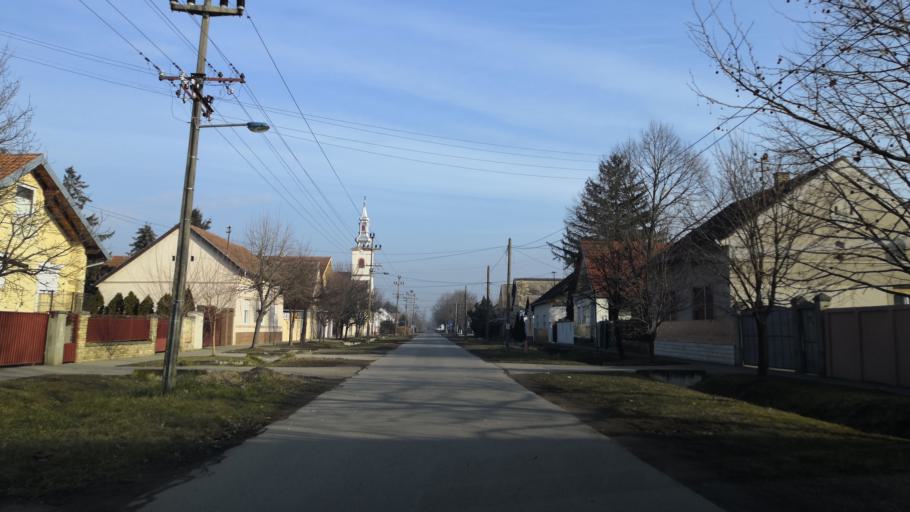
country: RS
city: Rumenka
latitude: 45.2942
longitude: 19.7459
